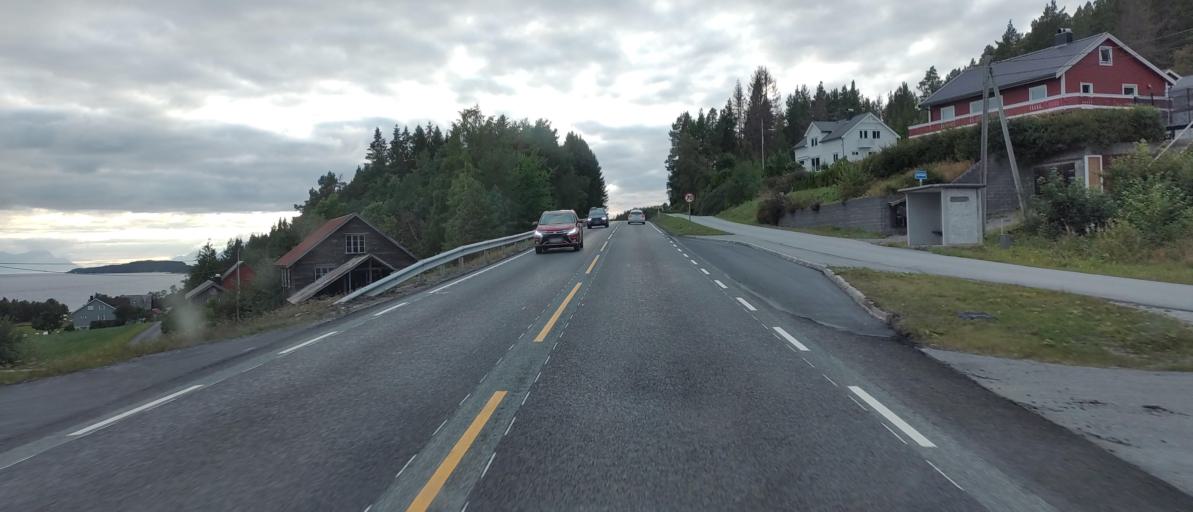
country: NO
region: More og Romsdal
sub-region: Molde
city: Hjelset
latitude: 62.7332
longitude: 7.4022
